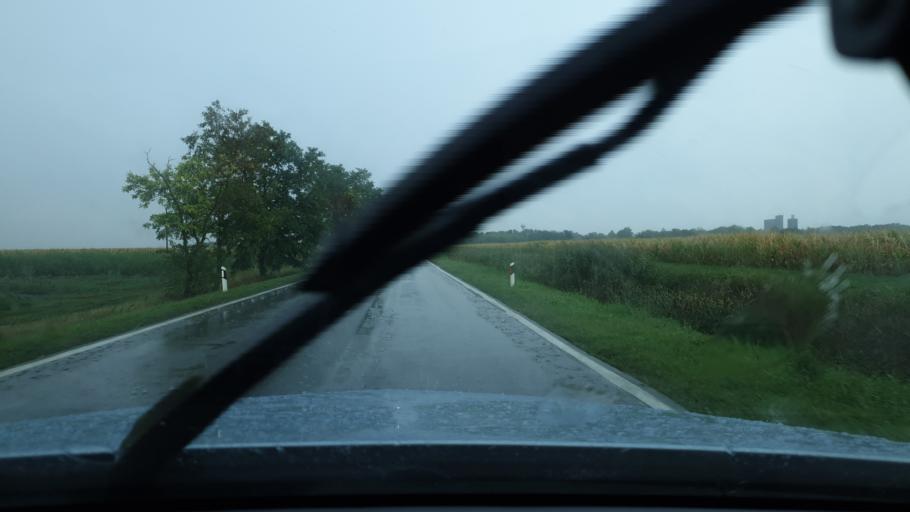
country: RS
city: Lazarevo
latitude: 45.3903
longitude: 20.5707
